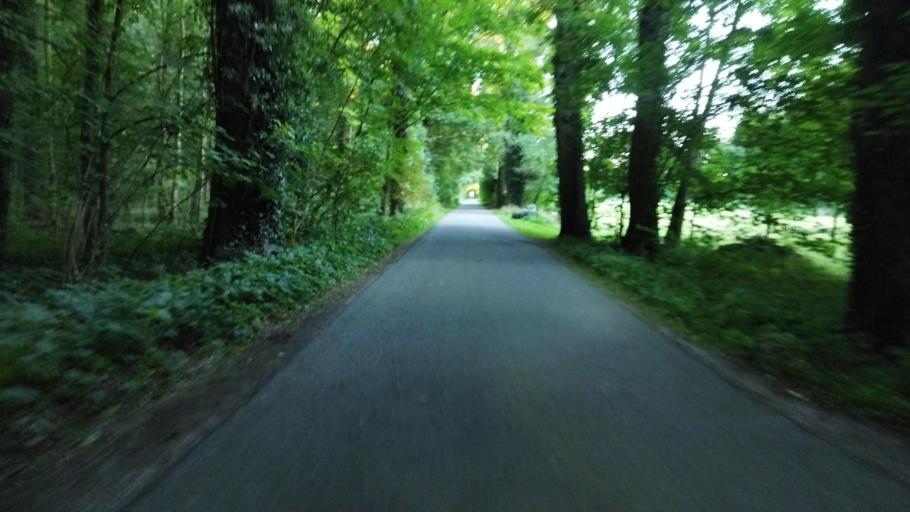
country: DE
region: Lower Saxony
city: Laar
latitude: 52.3677
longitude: 8.2443
